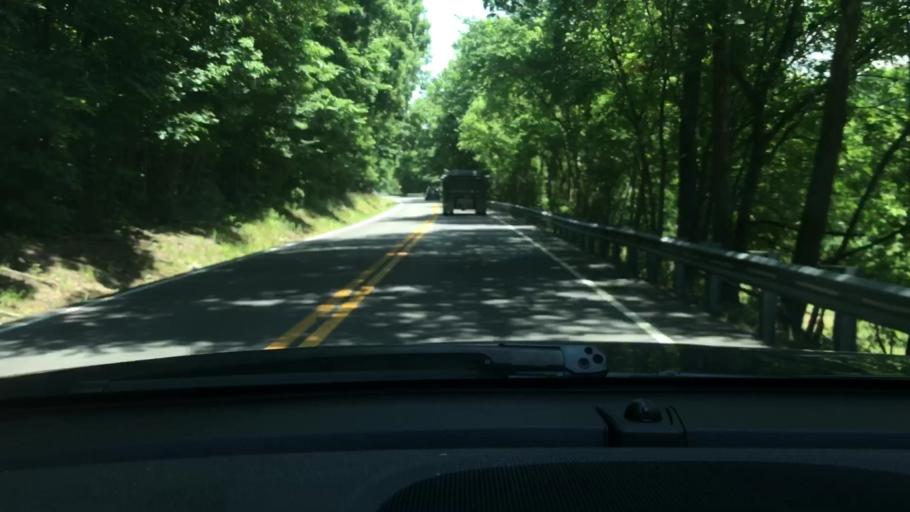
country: US
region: Tennessee
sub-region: Sumner County
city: White House
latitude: 36.4172
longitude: -86.6524
